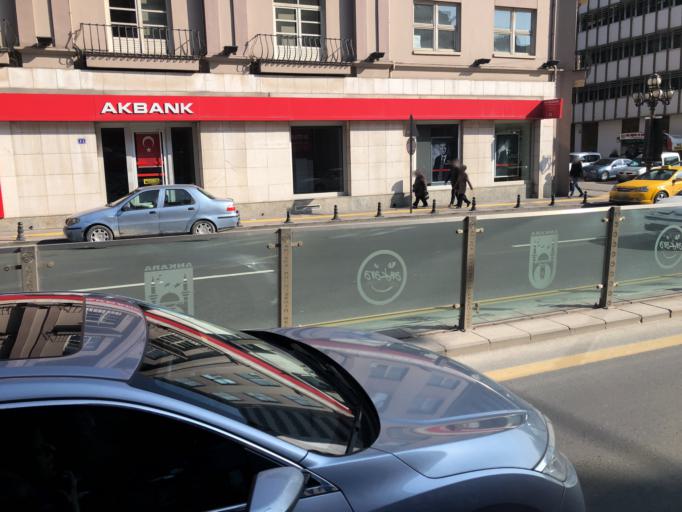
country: TR
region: Ankara
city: Ankara
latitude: 39.9406
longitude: 32.8543
